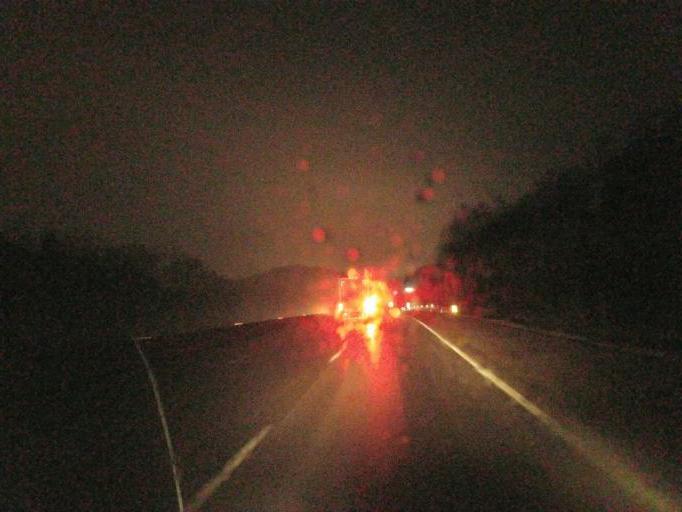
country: US
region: Missouri
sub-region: Franklin County
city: Pacific
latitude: 38.4923
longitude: -90.7364
